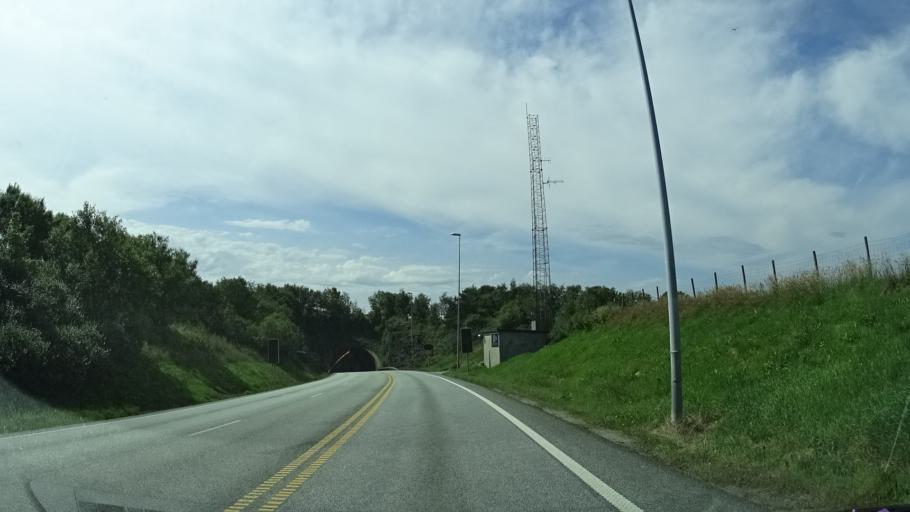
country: NO
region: Rogaland
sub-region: Rennesoy
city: Vikevag
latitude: 59.0556
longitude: 5.6580
